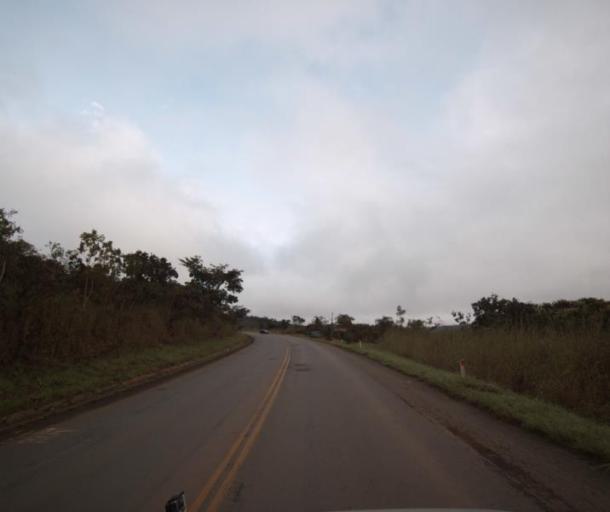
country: BR
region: Goias
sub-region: Pirenopolis
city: Pirenopolis
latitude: -15.8496
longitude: -48.7652
